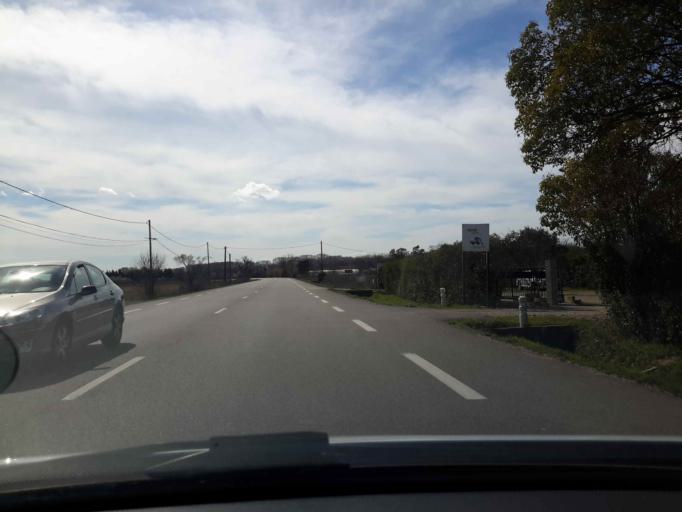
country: FR
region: Languedoc-Roussillon
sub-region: Departement du Gard
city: Vauvert
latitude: 43.7024
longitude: 4.2569
